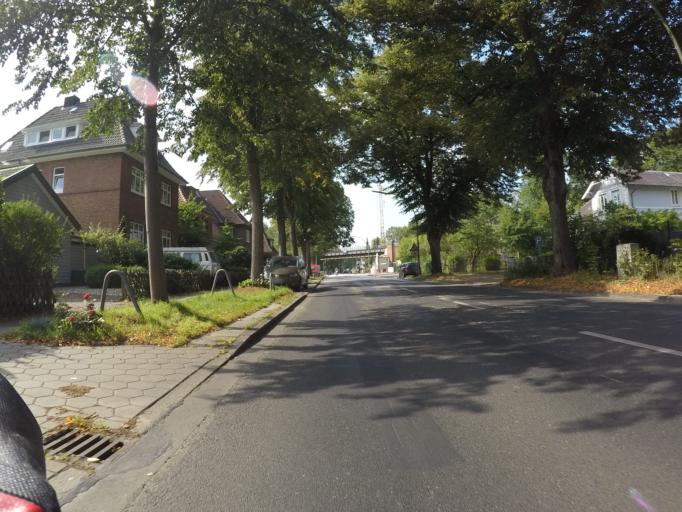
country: DE
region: Hamburg
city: Ohlsdorf
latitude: 53.6283
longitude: 10.0347
